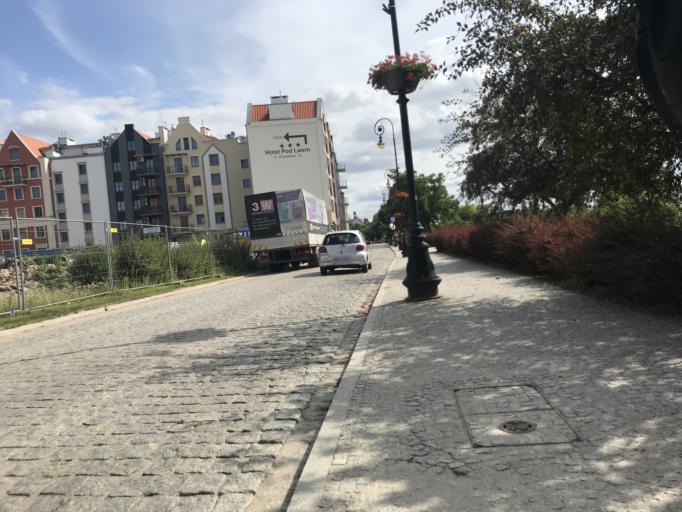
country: PL
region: Warmian-Masurian Voivodeship
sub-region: Powiat elblaski
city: Elblag
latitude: 54.1597
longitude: 19.3929
